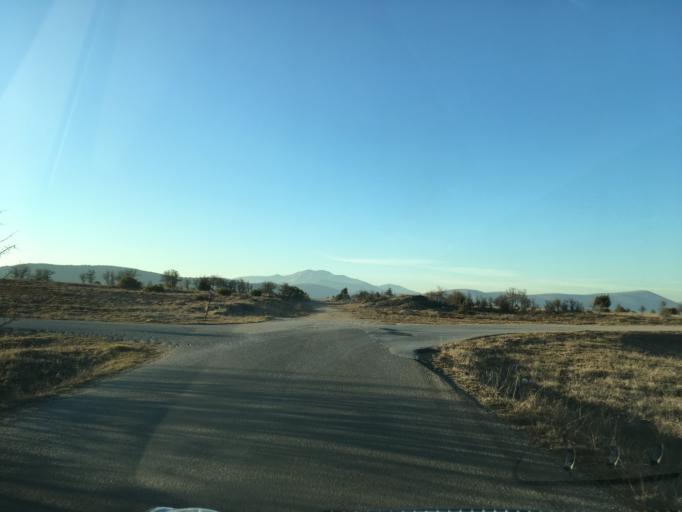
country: GR
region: West Macedonia
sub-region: Nomos Kozanis
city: Kozani
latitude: 40.2746
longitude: 21.7350
